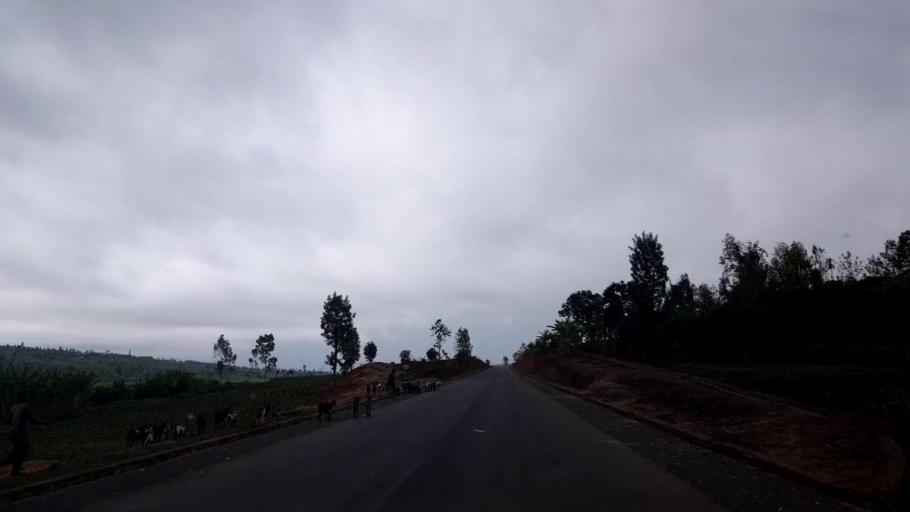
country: RW
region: Northern Province
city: Byumba
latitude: -1.4284
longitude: 30.2649
